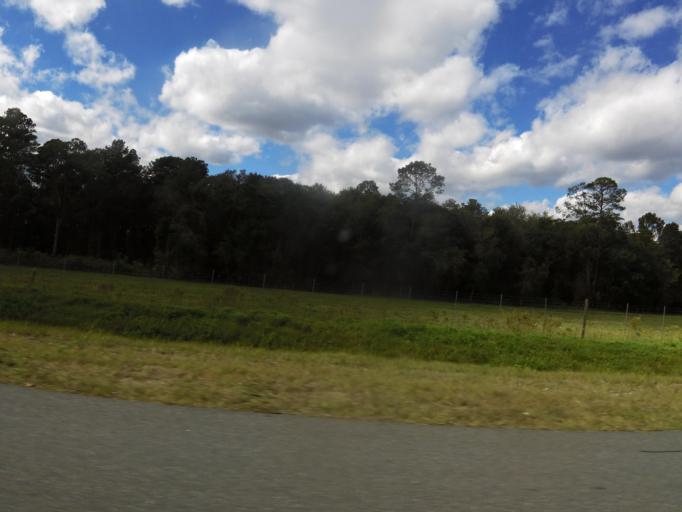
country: US
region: Florida
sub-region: Bradford County
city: Starke
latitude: 29.9582
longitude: -82.1358
